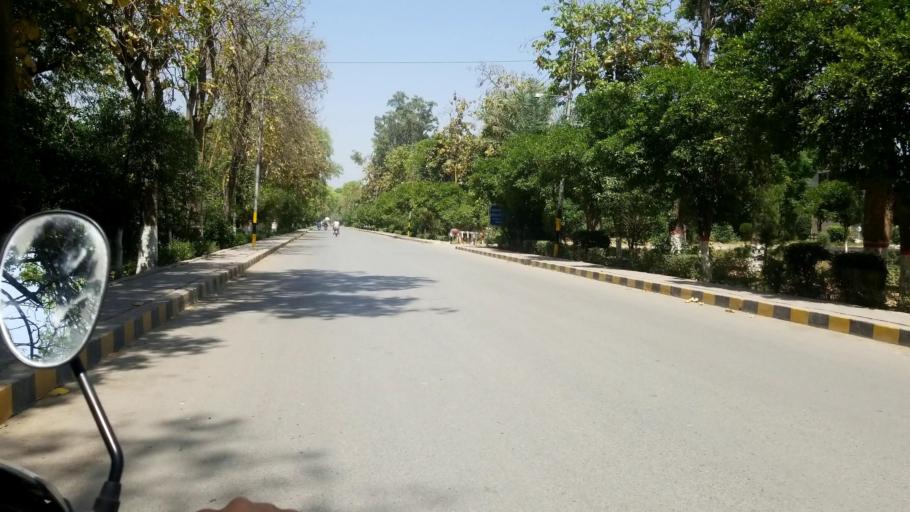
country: PK
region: Khyber Pakhtunkhwa
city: Peshawar
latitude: 34.0040
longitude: 71.4864
